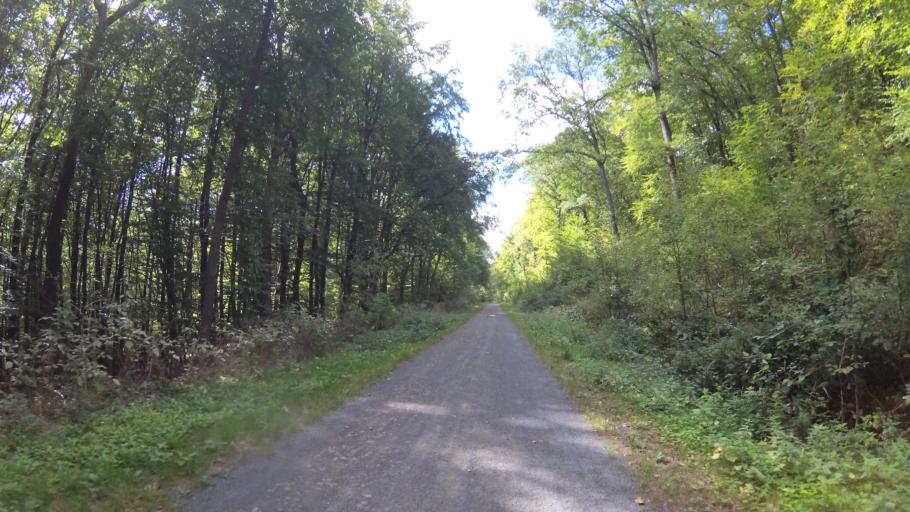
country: DE
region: Saarland
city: Freisen
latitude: 49.5355
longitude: 7.2469
